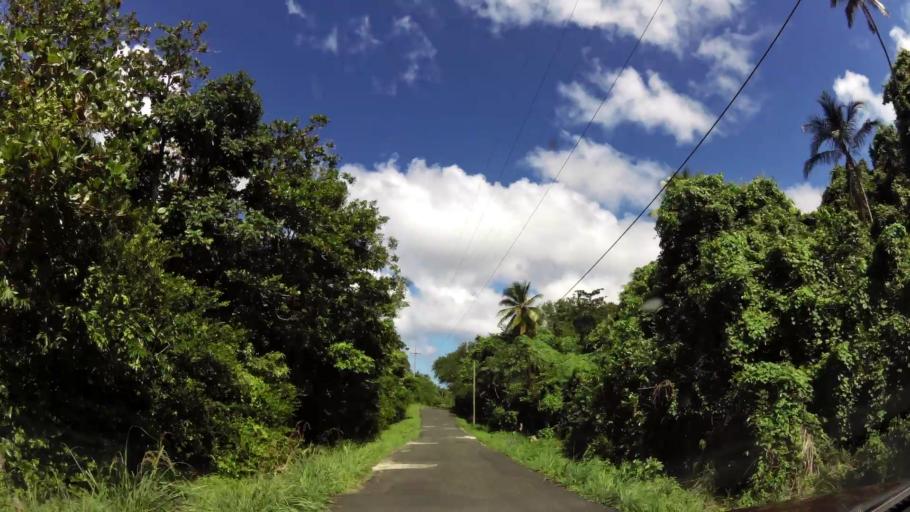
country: DM
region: Saint John
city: Portsmouth
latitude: 15.5908
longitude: -61.4637
